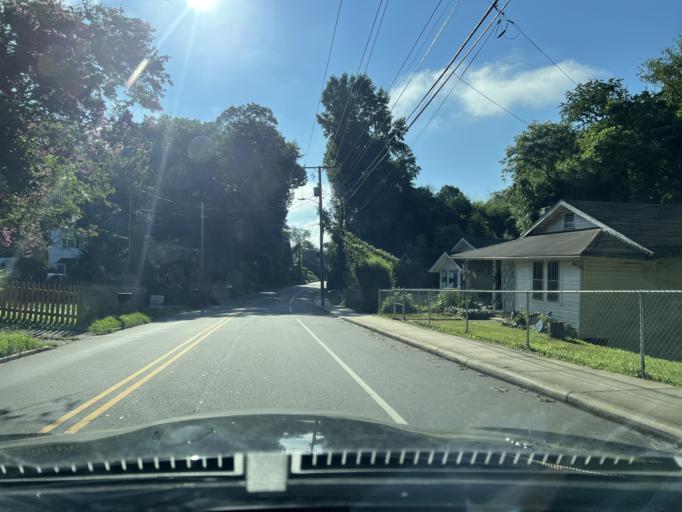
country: US
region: North Carolina
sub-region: Buncombe County
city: Asheville
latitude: 35.5709
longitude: -82.5813
